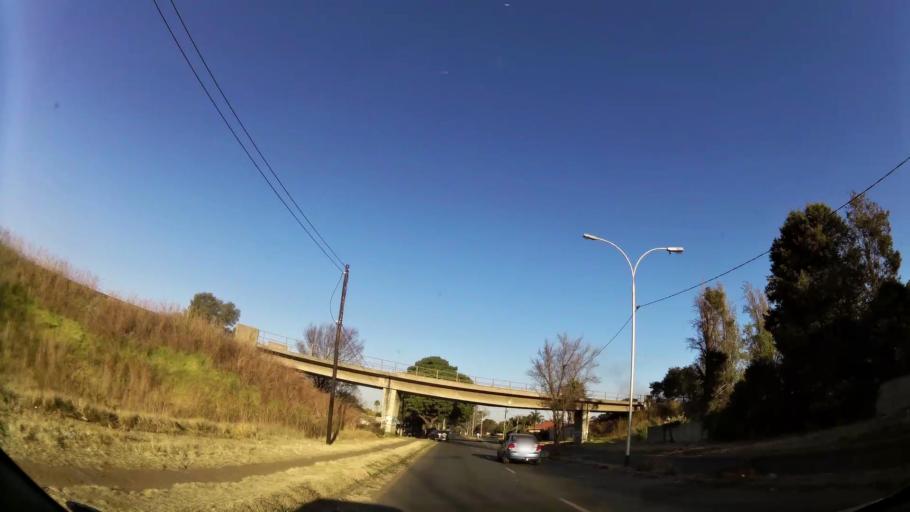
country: ZA
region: Gauteng
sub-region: City of Johannesburg Metropolitan Municipality
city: Roodepoort
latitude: -26.1659
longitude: 27.8757
